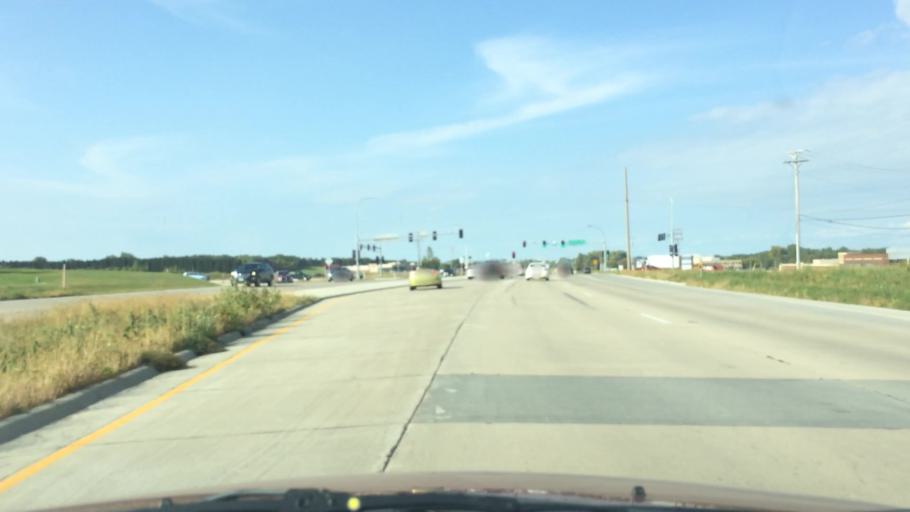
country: US
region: Minnesota
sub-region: Olmsted County
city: Rochester
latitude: 44.0566
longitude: -92.5238
